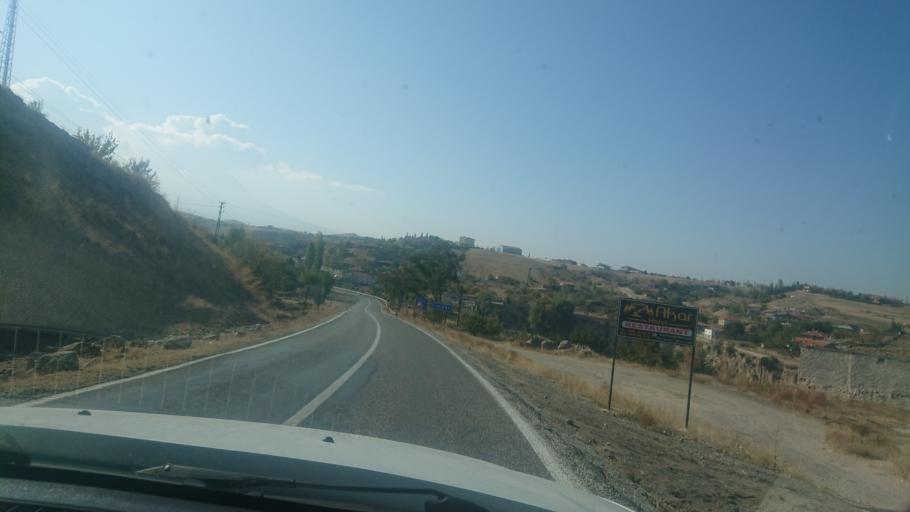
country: TR
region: Aksaray
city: Guzelyurt
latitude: 38.2445
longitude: 34.3119
